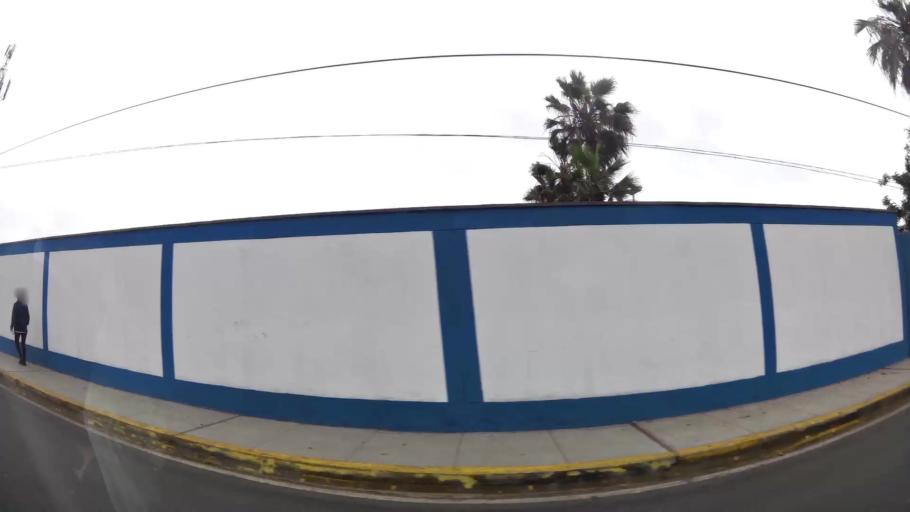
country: PE
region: Lima
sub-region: Lima
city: Surco
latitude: -12.1410
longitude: -77.0274
